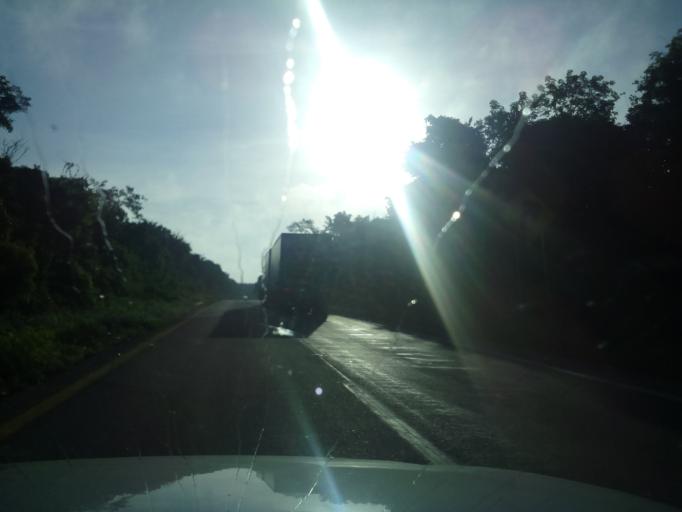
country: MX
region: Yucatan
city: Tunkas
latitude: 20.7656
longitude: -88.8028
